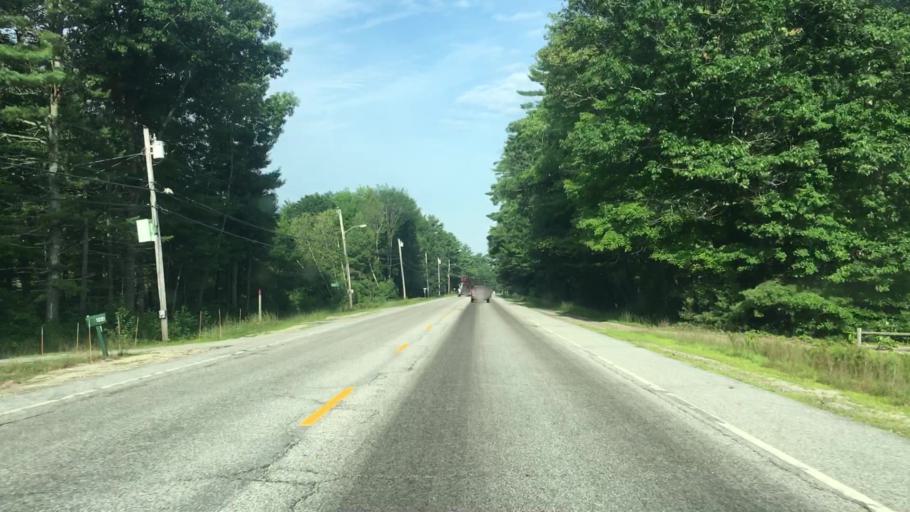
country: US
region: Maine
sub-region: Cumberland County
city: Steep Falls
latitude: 43.7321
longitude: -70.5957
